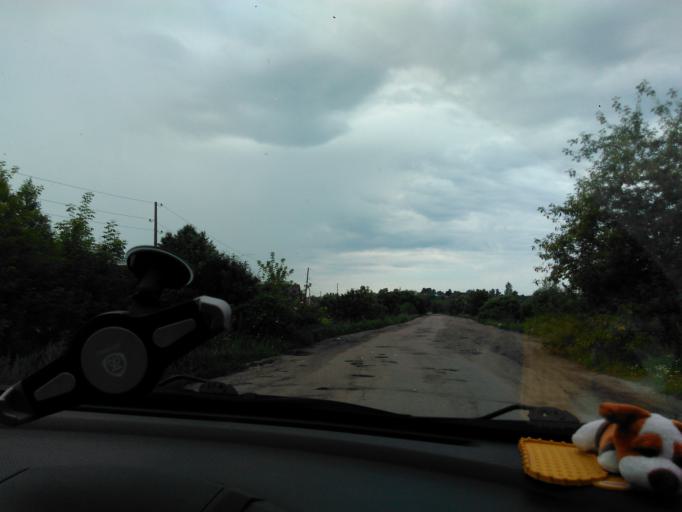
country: RU
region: Penza
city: Belinskiy
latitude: 52.9783
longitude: 43.4381
